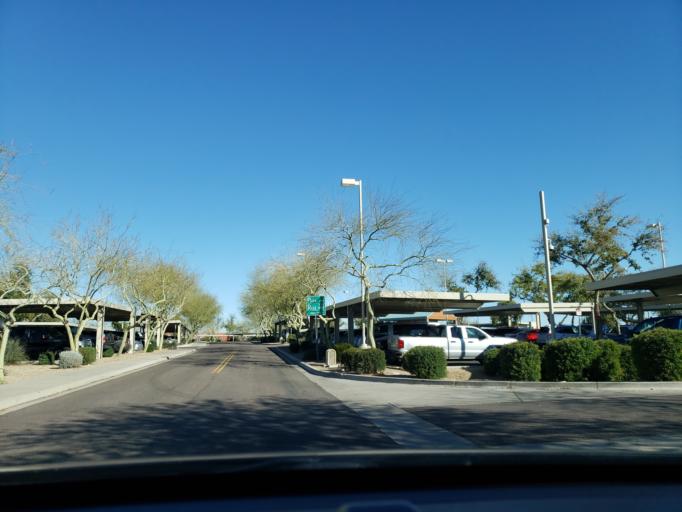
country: US
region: Arizona
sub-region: Maricopa County
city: Glendale
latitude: 33.6381
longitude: -112.1180
